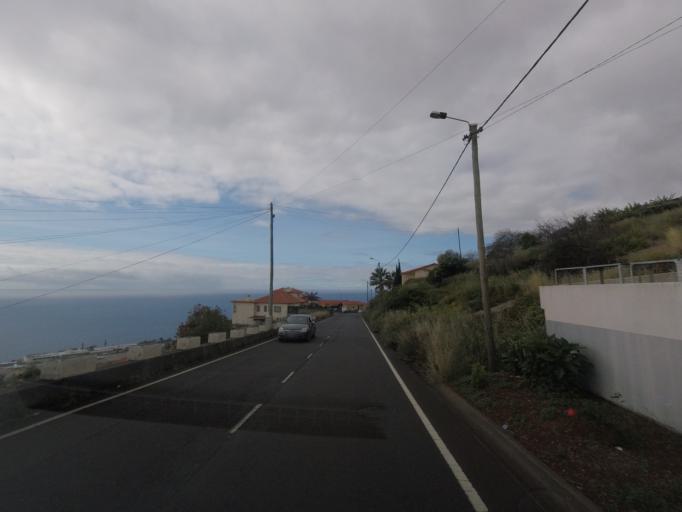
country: PT
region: Madeira
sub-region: Machico
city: Machico
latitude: 32.7022
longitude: -16.7809
